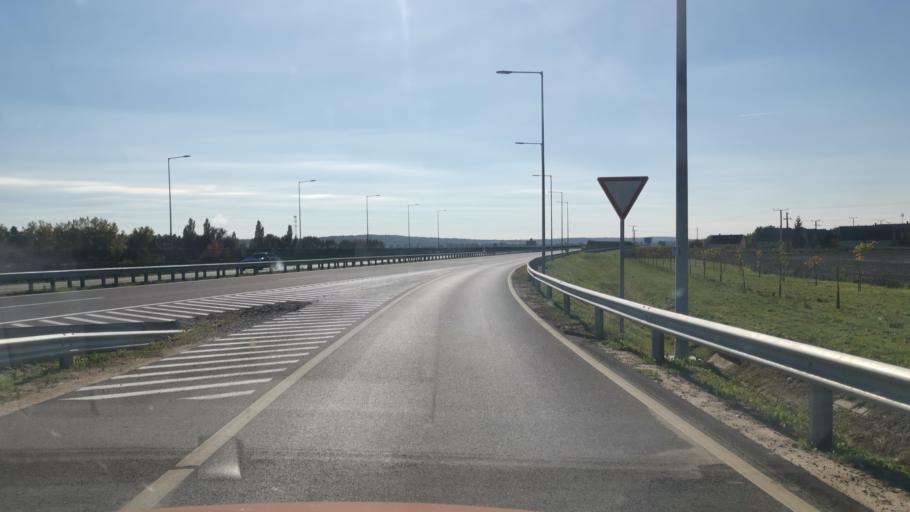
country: HU
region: Borsod-Abauj-Zemplen
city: Encs
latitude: 48.3304
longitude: 21.1024
